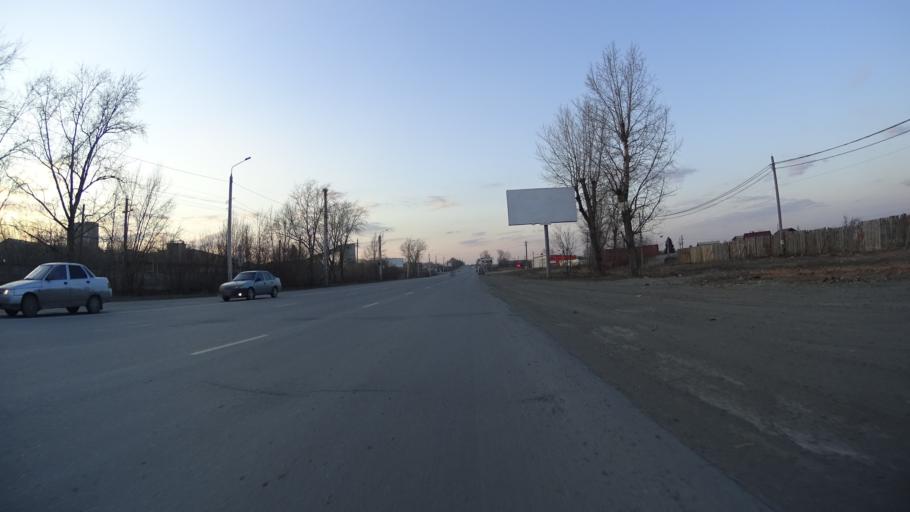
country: RU
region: Chelyabinsk
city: Novosineglazovskiy
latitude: 55.0954
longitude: 61.3881
